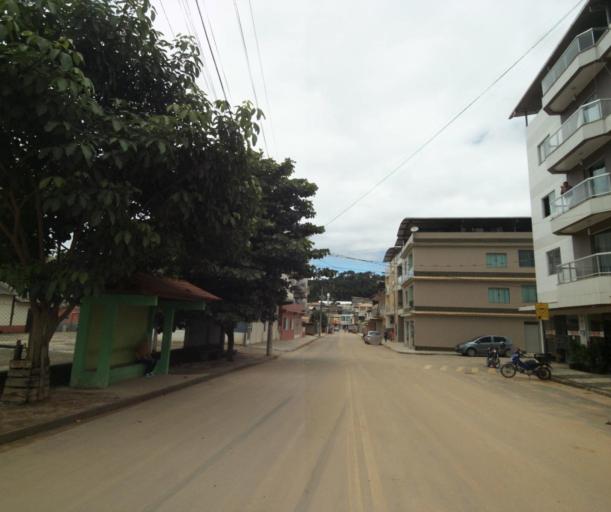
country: BR
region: Espirito Santo
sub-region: Irupi
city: Irupi
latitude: -20.3424
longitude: -41.6430
